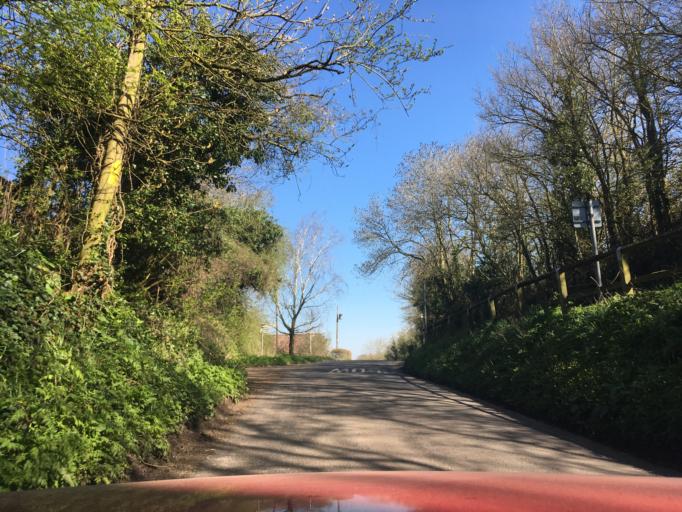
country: GB
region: England
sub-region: South Gloucestershire
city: Hill
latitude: 51.6716
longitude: -2.5013
